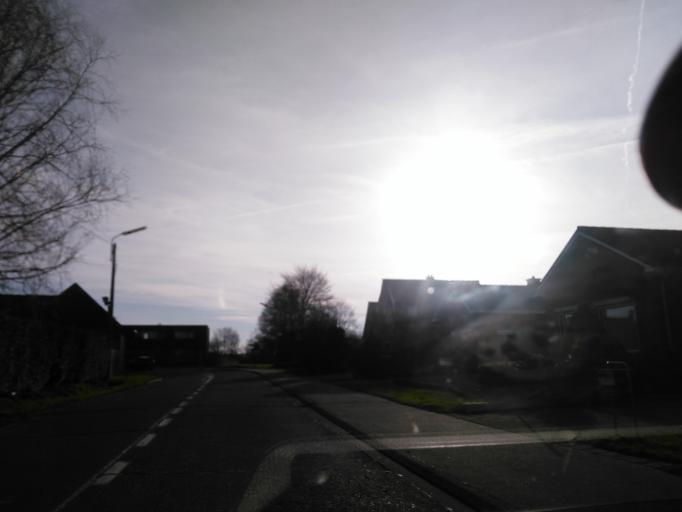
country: BE
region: Flanders
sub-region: Provincie Oost-Vlaanderen
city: Sint-Gillis-Waas
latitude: 51.2187
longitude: 4.1724
